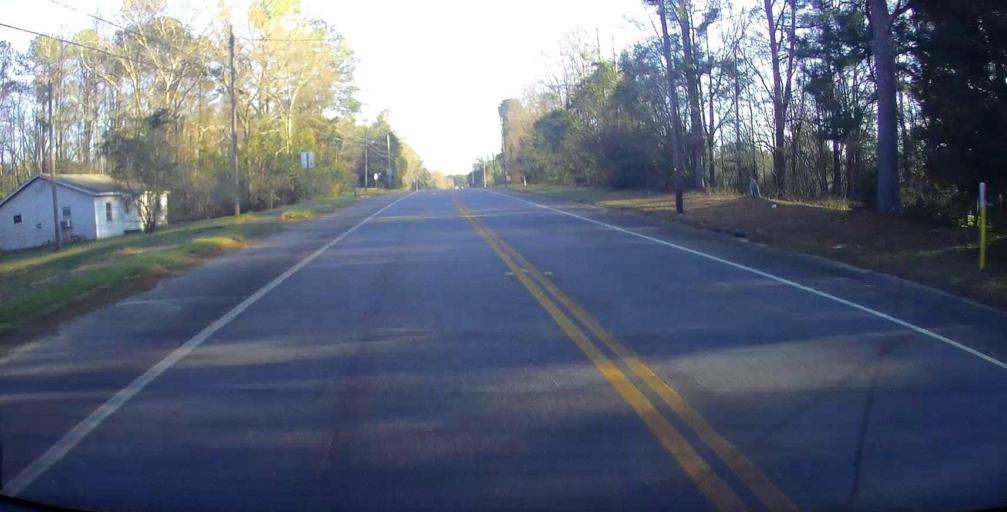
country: US
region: Georgia
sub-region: Talbot County
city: Talbotton
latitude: 32.6654
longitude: -84.5337
